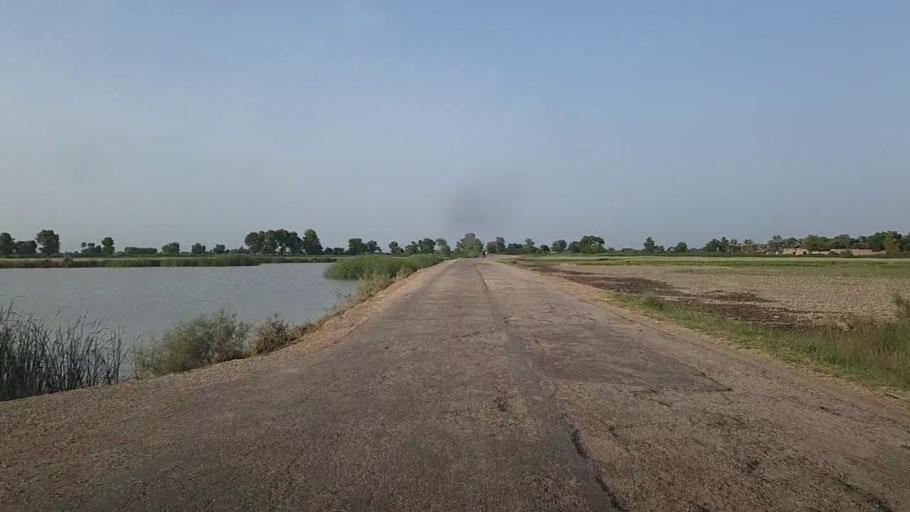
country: PK
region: Sindh
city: Ubauro
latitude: 28.0971
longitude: 69.8086
